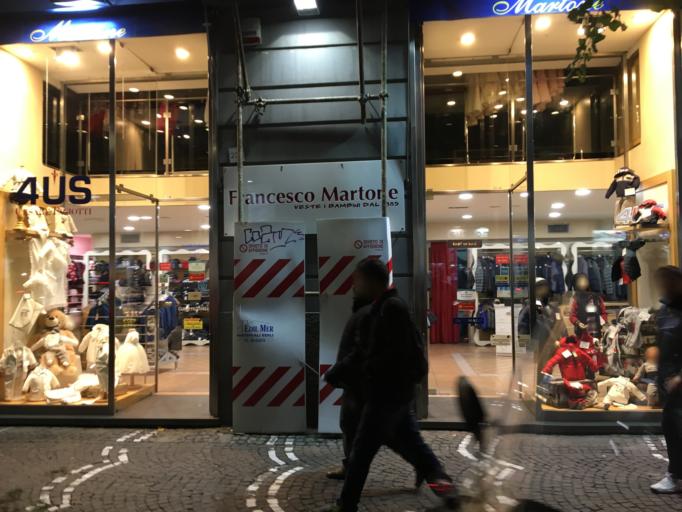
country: IT
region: Campania
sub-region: Provincia di Napoli
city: Napoli
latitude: 40.8499
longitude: 14.2653
